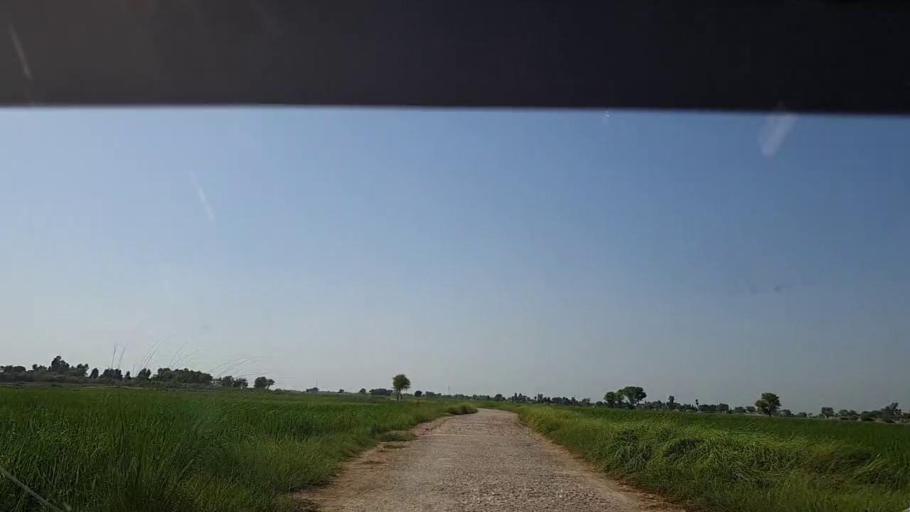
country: PK
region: Sindh
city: Ghauspur
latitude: 28.1800
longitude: 69.0320
